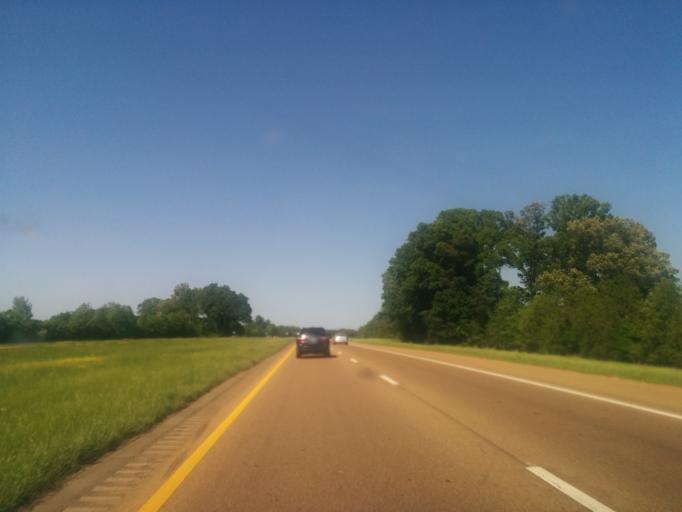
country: US
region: Mississippi
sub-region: Madison County
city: Madison
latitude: 32.4943
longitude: -90.1245
